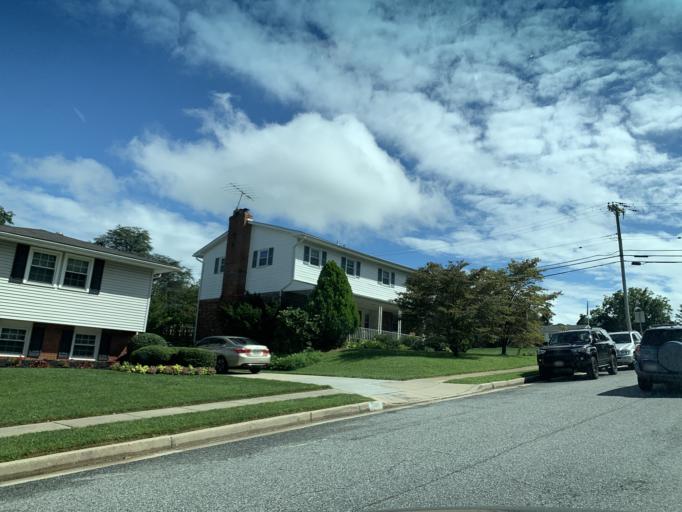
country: US
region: Maryland
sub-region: Baltimore County
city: Timonium
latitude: 39.4513
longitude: -76.6142
